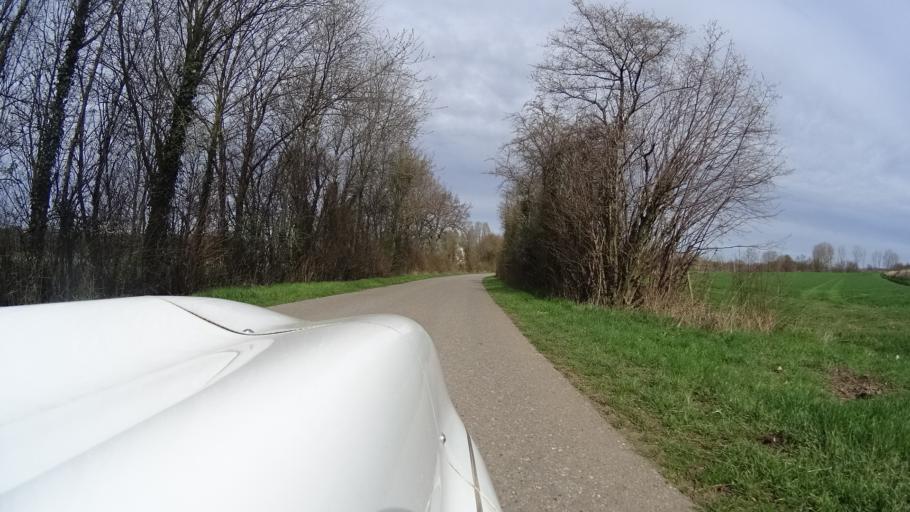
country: NL
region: Limburg
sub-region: Gemeente Gennep
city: Gennep
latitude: 51.6938
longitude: 6.0339
